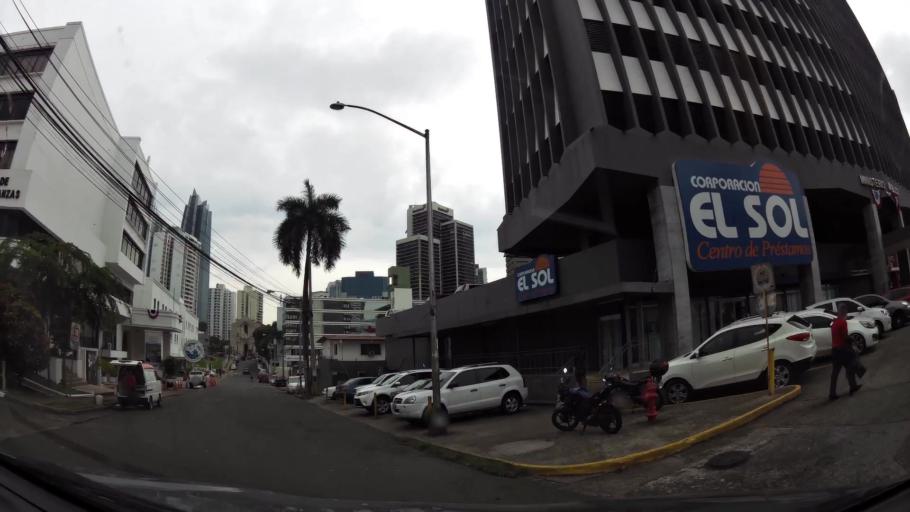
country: PA
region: Panama
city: Panama
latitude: 8.9859
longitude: -79.5243
